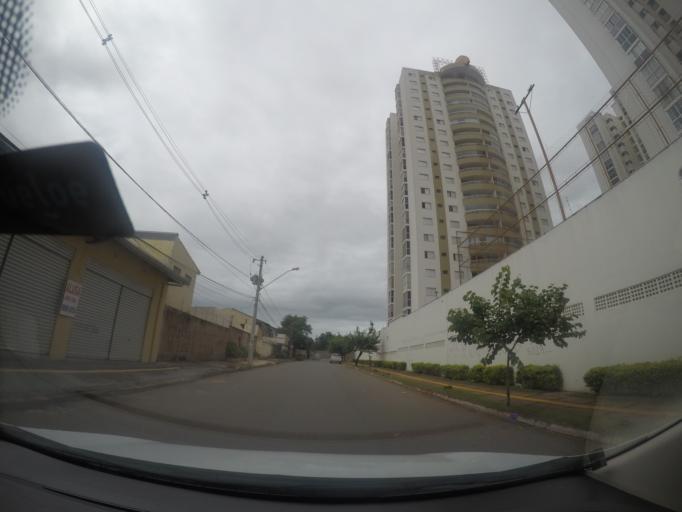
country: BR
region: Goias
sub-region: Goiania
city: Goiania
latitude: -16.7100
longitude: -49.3263
